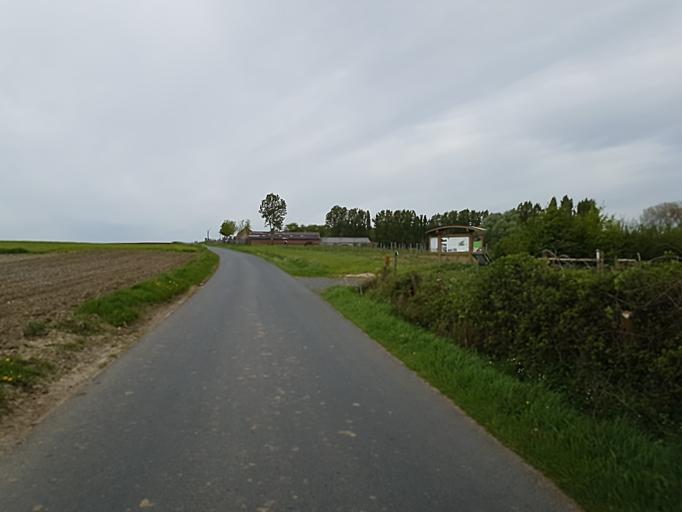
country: BE
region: Flanders
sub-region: Provincie West-Vlaanderen
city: Zonnebeke
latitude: 50.8485
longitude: 2.9975
